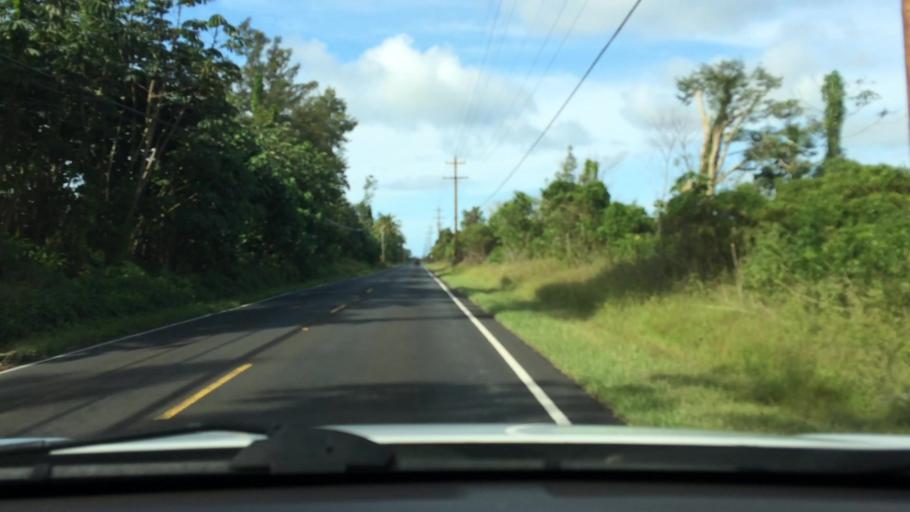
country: US
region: Hawaii
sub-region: Hawaii County
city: Nanawale Estates
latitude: 19.5140
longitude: -154.9405
